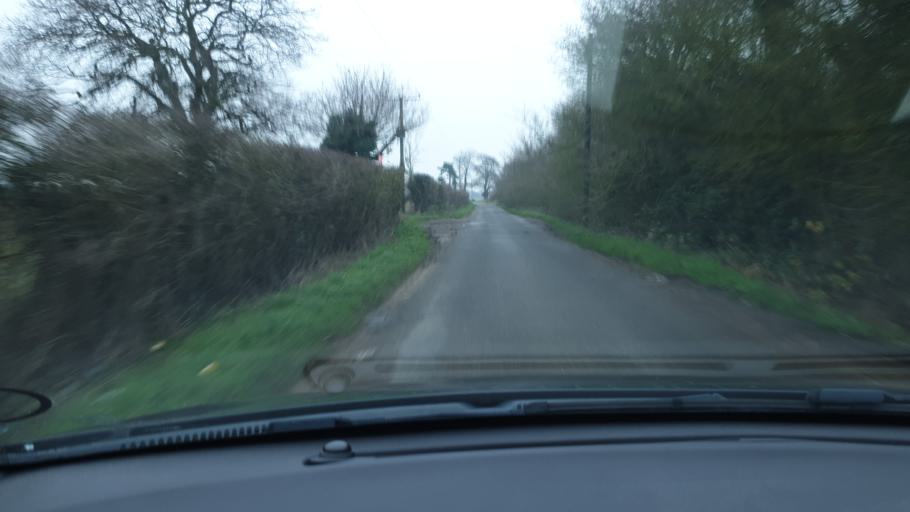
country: GB
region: England
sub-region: Essex
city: Great Bentley
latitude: 51.8345
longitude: 1.0792
